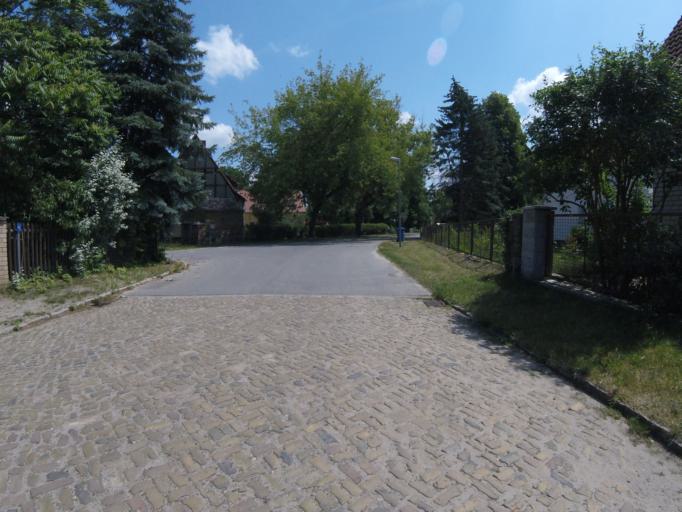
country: DE
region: Brandenburg
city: Bestensee
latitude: 52.2576
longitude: 13.7316
